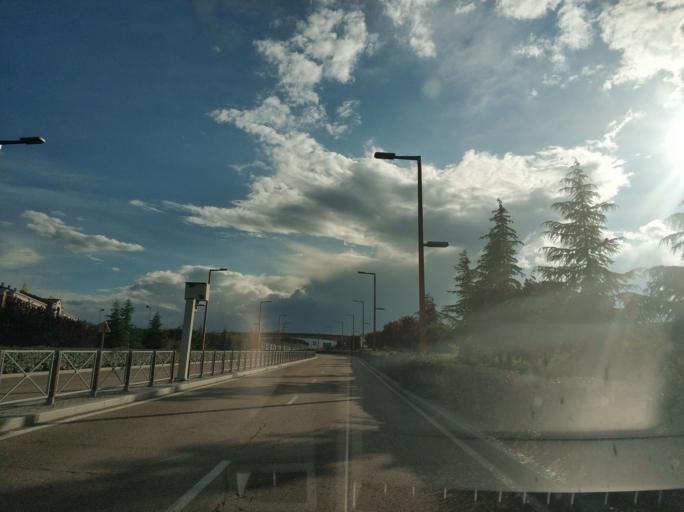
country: ES
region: Castille and Leon
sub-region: Provincia de Valladolid
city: Arroyo
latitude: 41.6195
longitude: -4.7825
